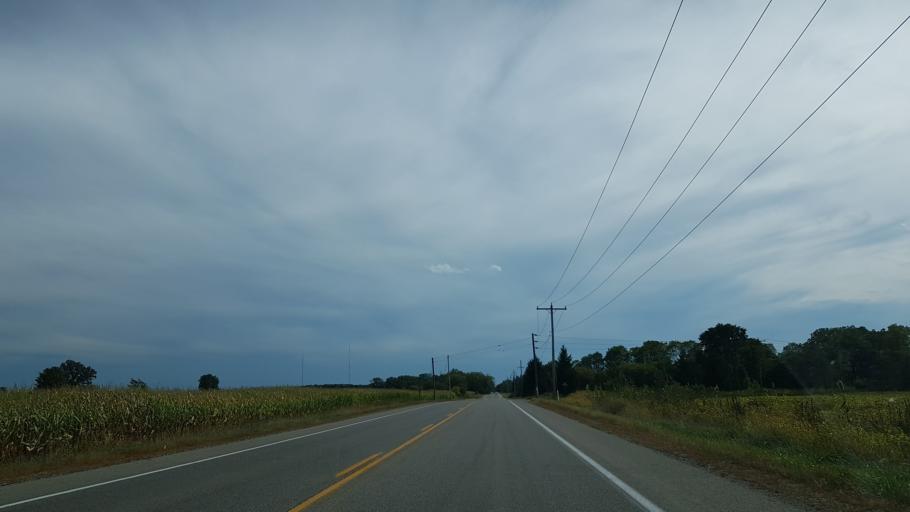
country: CA
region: Ontario
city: Delaware
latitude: 42.9928
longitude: -81.3922
